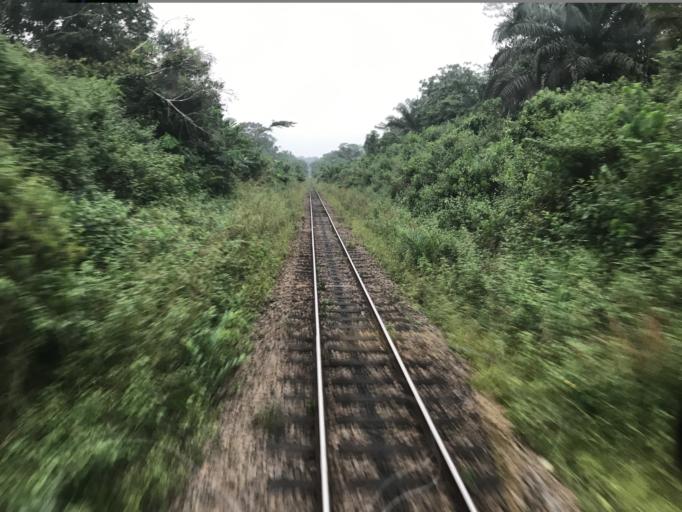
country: CM
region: Littoral
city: Edea
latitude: 3.9770
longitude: 10.0681
